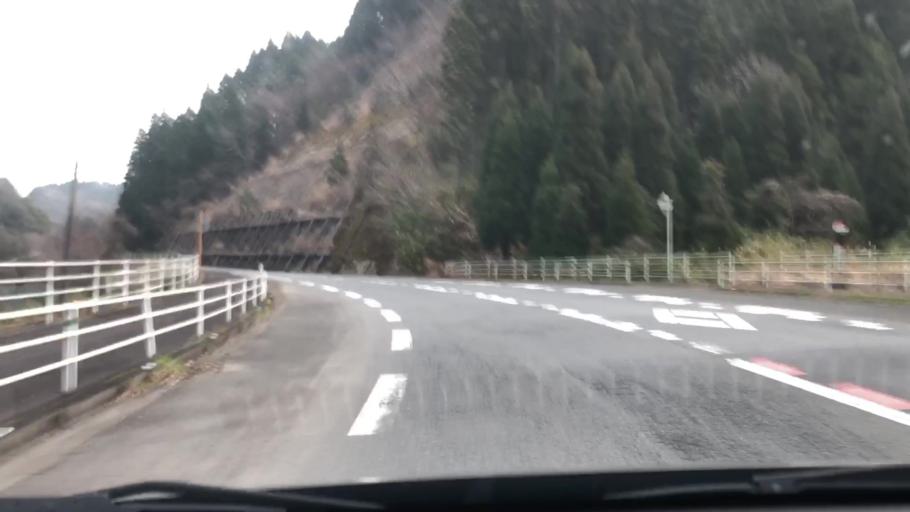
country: JP
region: Oita
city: Takedamachi
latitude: 32.9775
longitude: 131.5478
